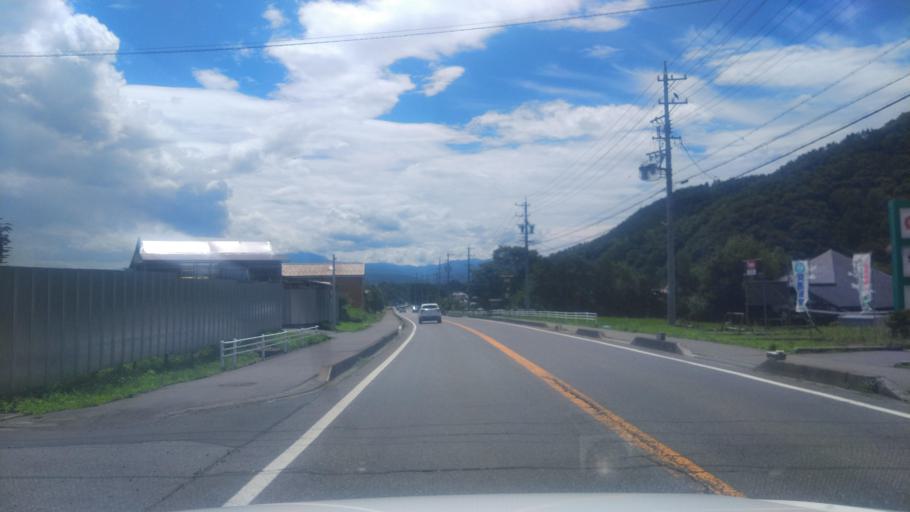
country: JP
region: Nagano
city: Ueda
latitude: 36.4333
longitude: 138.2988
